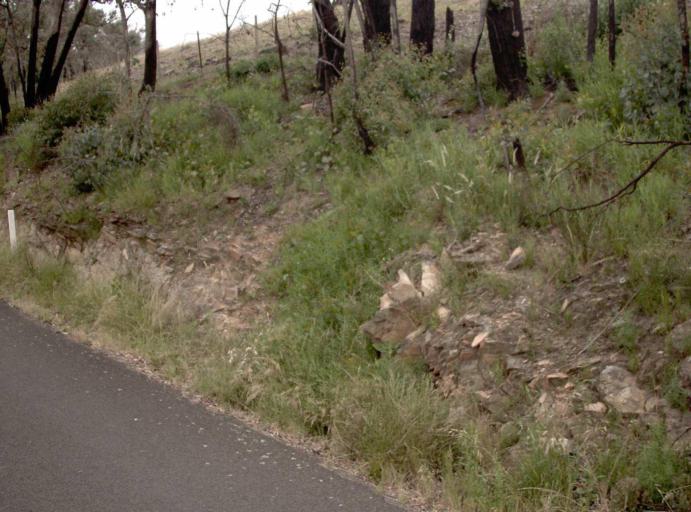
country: AU
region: Victoria
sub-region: Wellington
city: Heyfield
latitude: -37.8468
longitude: 146.7081
